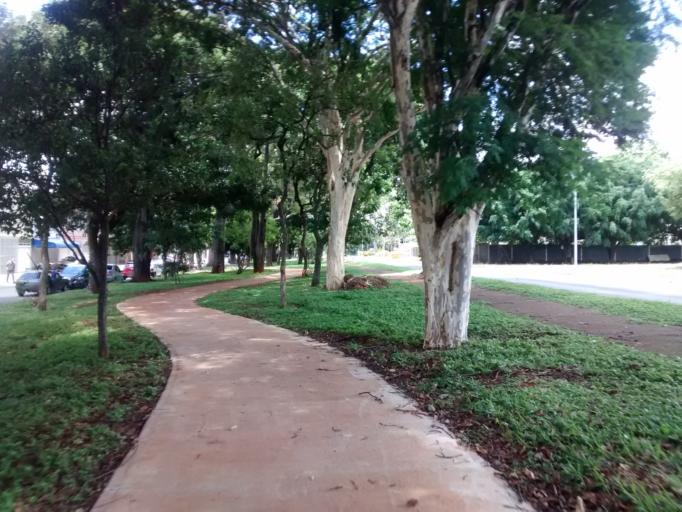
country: BR
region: Federal District
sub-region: Brasilia
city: Brasilia
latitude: -15.8084
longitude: -47.9052
